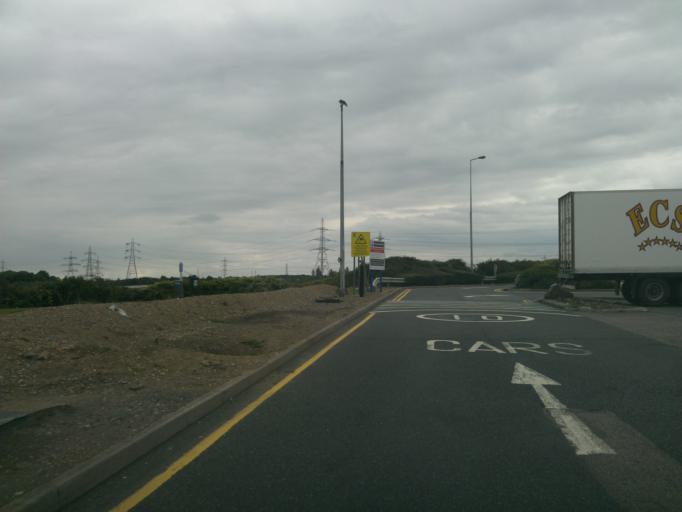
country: GB
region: England
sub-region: Kent
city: West Thurrock
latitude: 51.4940
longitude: 0.2718
